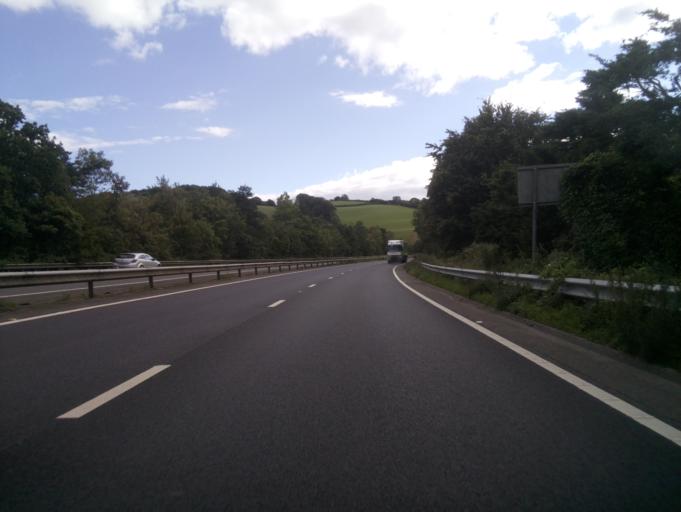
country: GB
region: England
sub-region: Devon
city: Buckfastleigh
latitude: 50.4822
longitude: -3.7699
